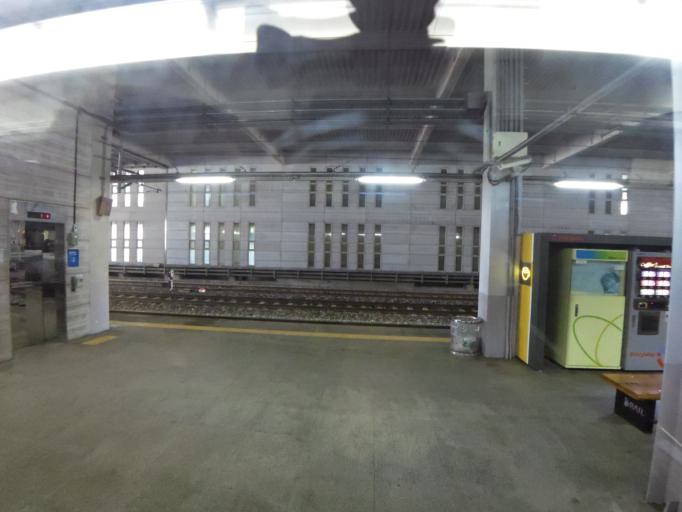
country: KR
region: Gyeongsangbuk-do
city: Gumi
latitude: 36.1287
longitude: 128.3312
